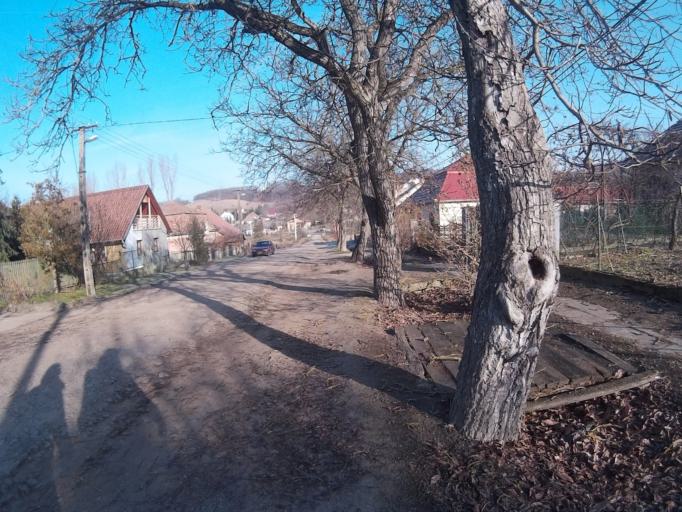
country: HU
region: Nograd
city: Bercel
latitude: 47.9260
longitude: 19.4102
